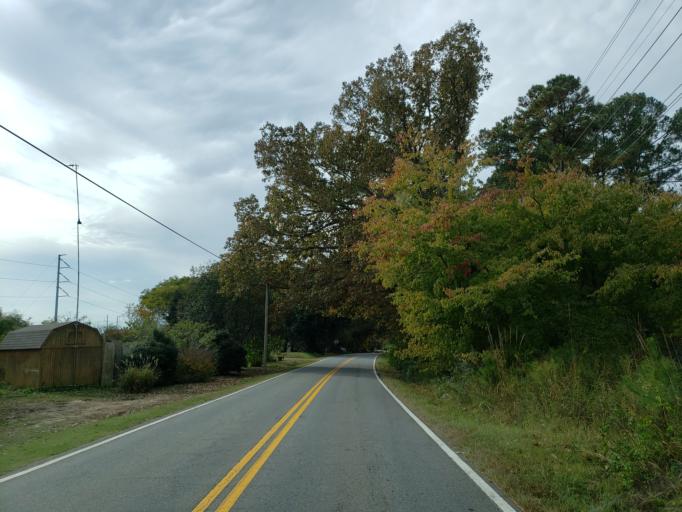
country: US
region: Georgia
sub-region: Cobb County
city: Acworth
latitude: 34.0632
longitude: -84.6448
